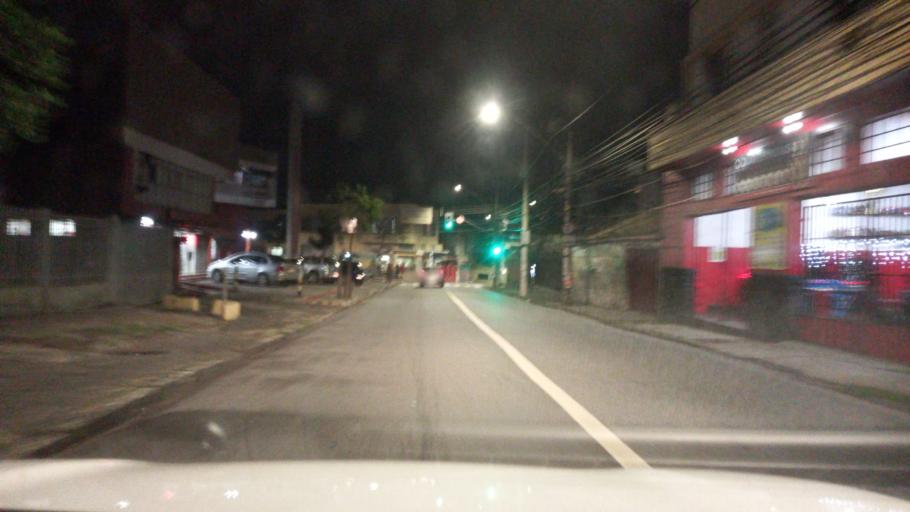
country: BR
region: Minas Gerais
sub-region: Belo Horizonte
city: Belo Horizonte
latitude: -19.9117
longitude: -43.9634
